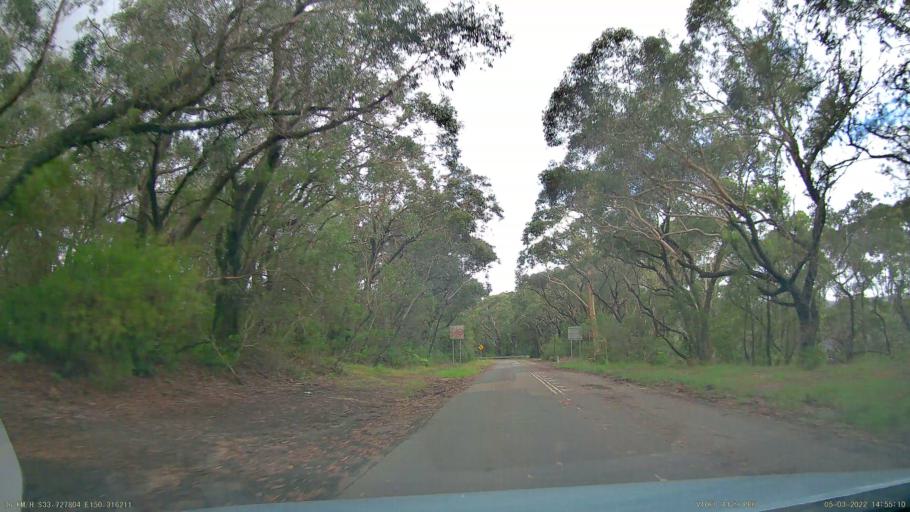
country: AU
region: New South Wales
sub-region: Blue Mountains Municipality
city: Katoomba
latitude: -33.7277
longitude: 150.3164
